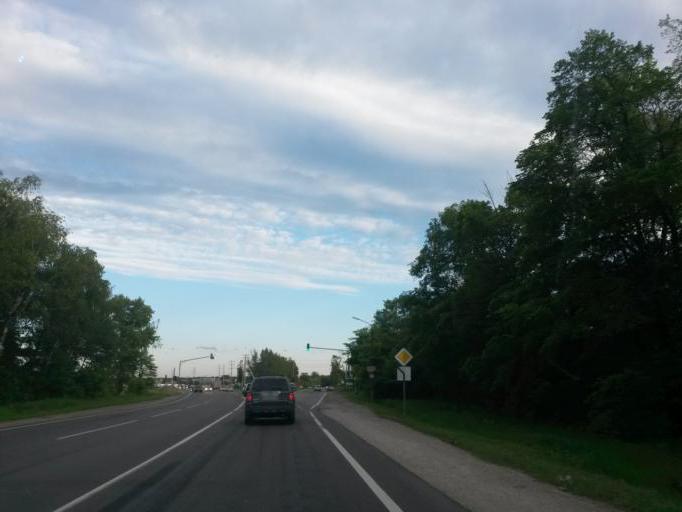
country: RU
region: Moskovskaya
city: Barybino
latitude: 55.2053
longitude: 37.8689
